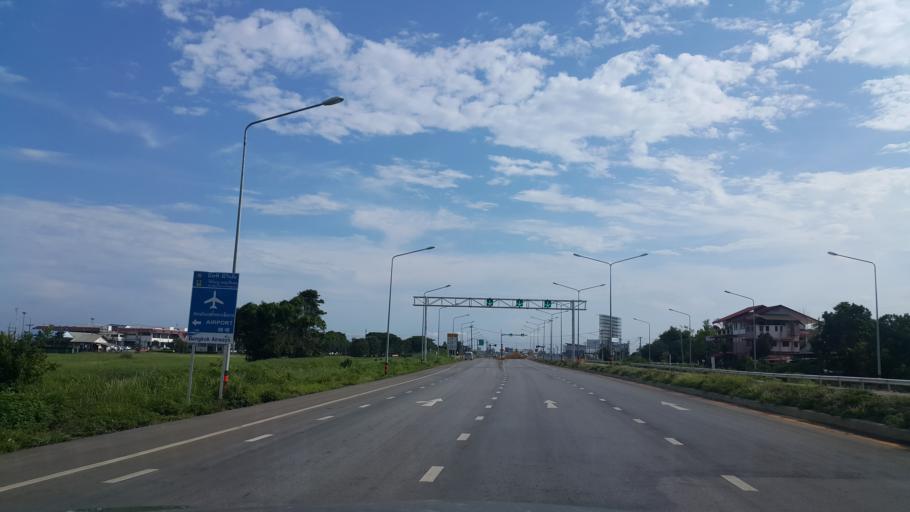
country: TH
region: Chiang Rai
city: Chiang Rai
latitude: 19.9594
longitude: 99.8797
